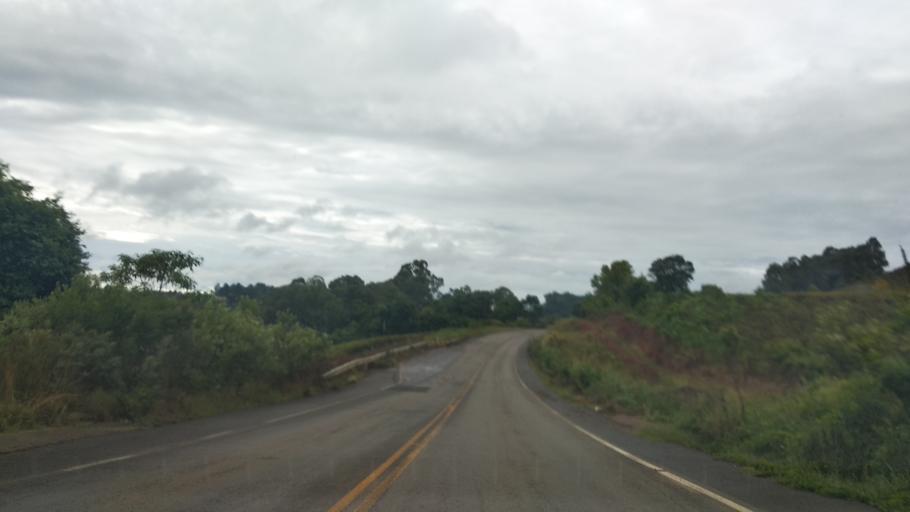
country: BR
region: Santa Catarina
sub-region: Videira
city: Videira
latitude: -27.0225
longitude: -51.1629
